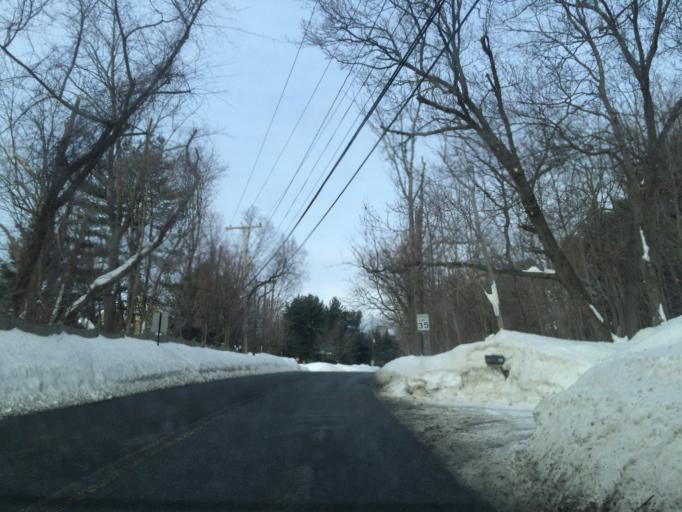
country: US
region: Massachusetts
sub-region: Middlesex County
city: Weston
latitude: 42.3383
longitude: -71.2890
